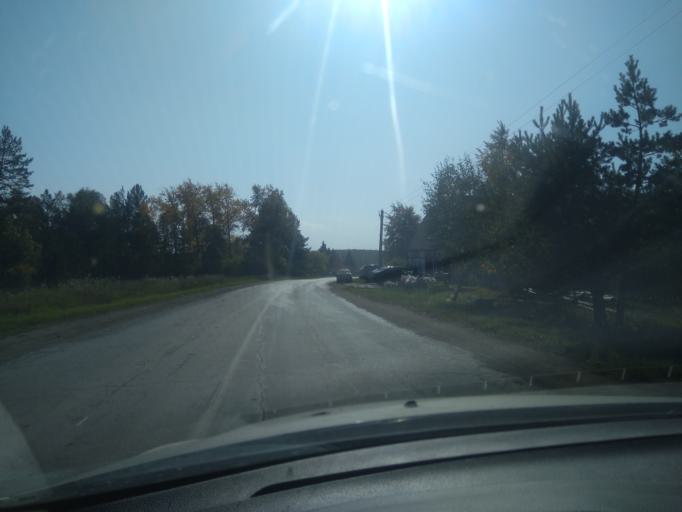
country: RU
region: Sverdlovsk
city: Pokrovskoye
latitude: 56.4437
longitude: 61.6029
